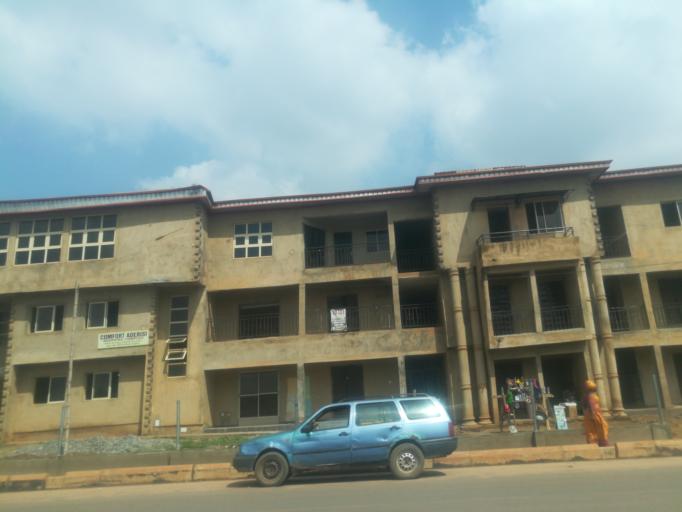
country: NG
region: Oyo
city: Ibadan
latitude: 7.3901
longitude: 3.9430
